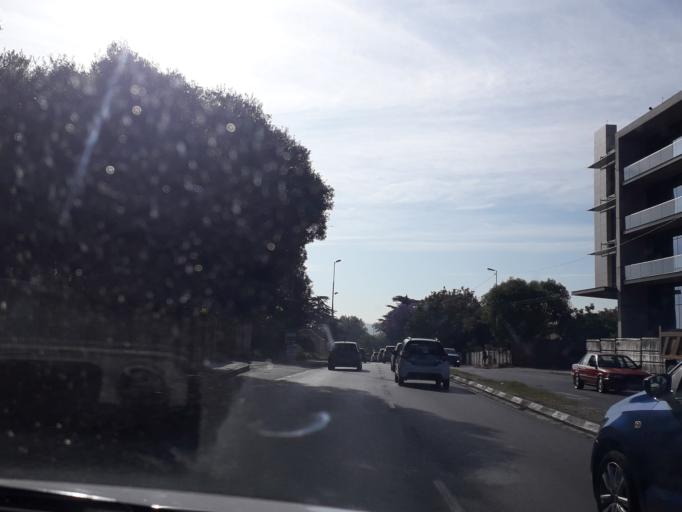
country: ZA
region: Gauteng
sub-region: City of Johannesburg Metropolitan Municipality
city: Johannesburg
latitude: -26.1002
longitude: 28.0029
